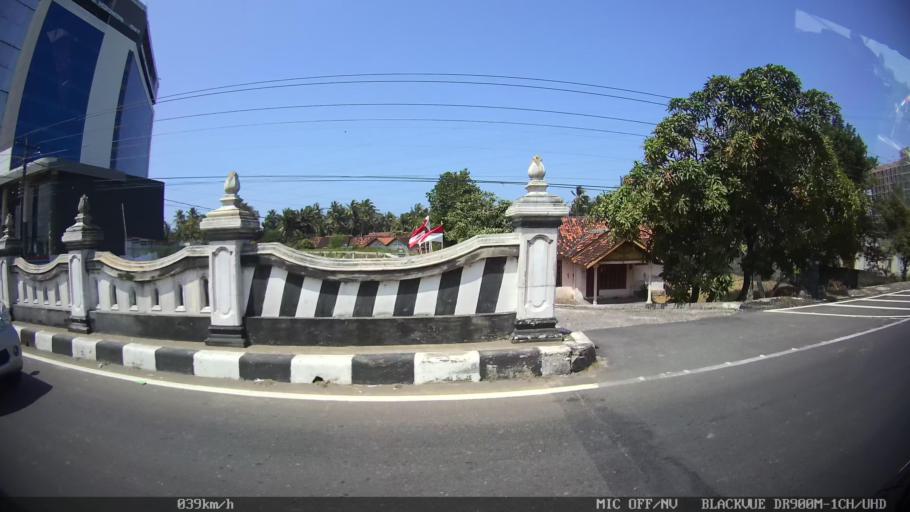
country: ID
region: Daerah Istimewa Yogyakarta
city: Srandakan
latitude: -7.8867
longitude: 110.0720
